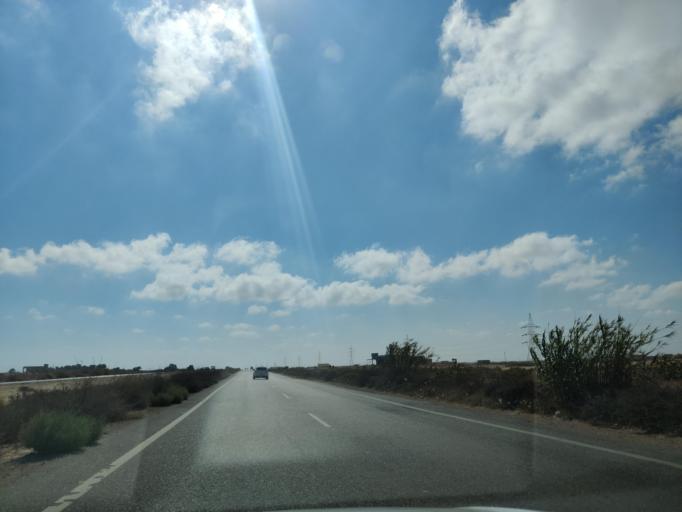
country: EG
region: Muhafazat Matruh
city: Al `Alamayn
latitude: 31.0541
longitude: 28.2700
